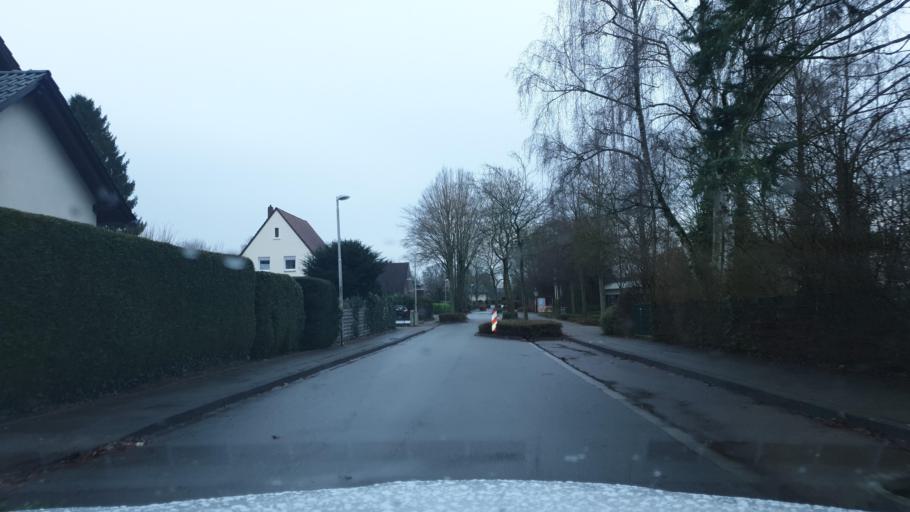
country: DE
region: North Rhine-Westphalia
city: Bad Oeynhausen
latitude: 52.2580
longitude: 8.7496
